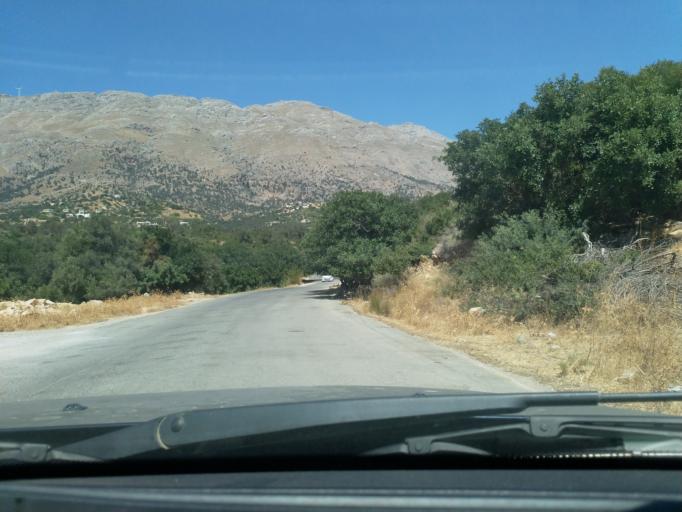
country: GR
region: Crete
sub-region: Nomos Rethymnis
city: Agia Galini
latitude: 35.1235
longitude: 24.5590
